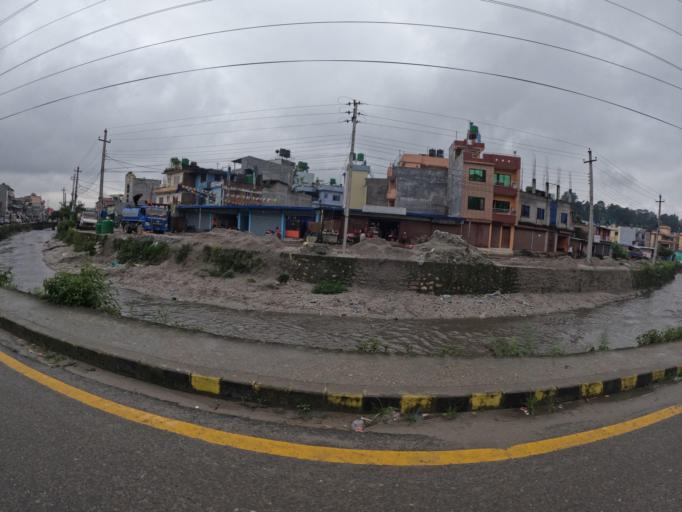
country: NP
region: Central Region
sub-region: Bagmati Zone
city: Kathmandu
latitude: 27.7514
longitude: 85.3167
